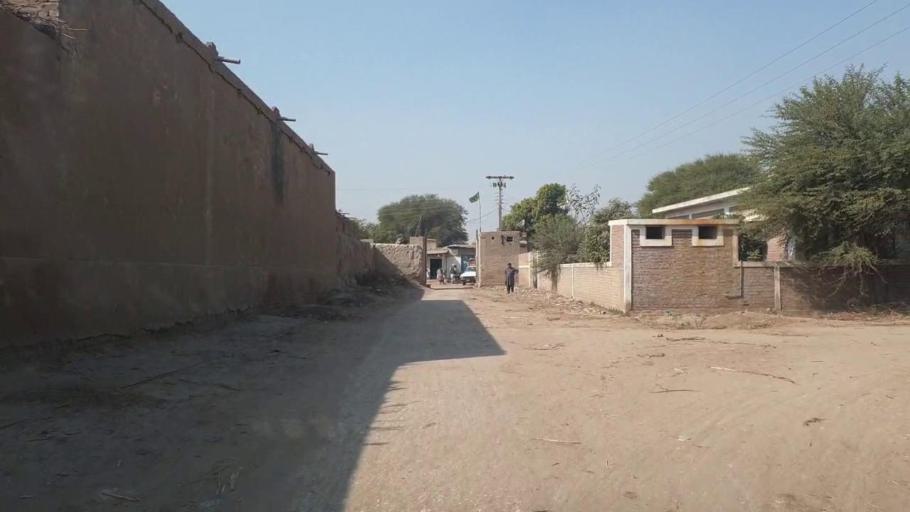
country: PK
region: Sindh
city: Tando Jam
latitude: 25.3322
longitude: 68.6285
